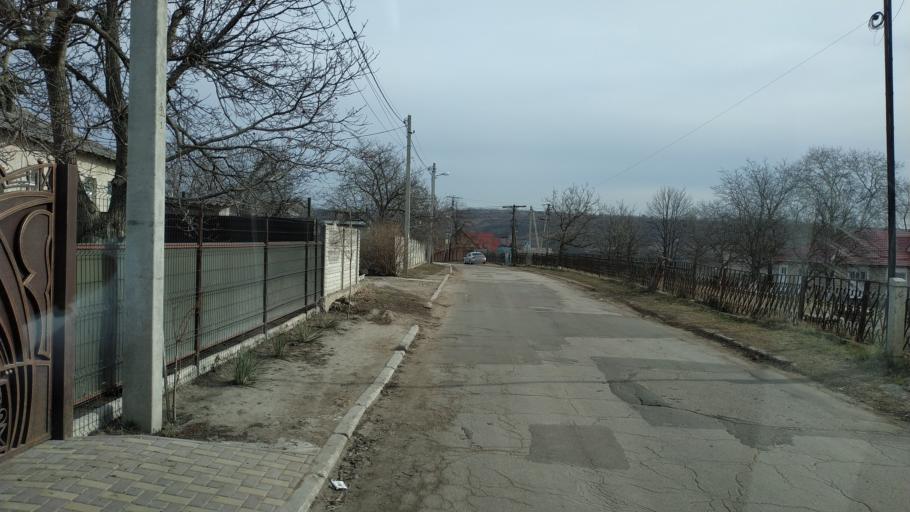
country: MD
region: Chisinau
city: Vatra
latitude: 47.0955
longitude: 28.7644
